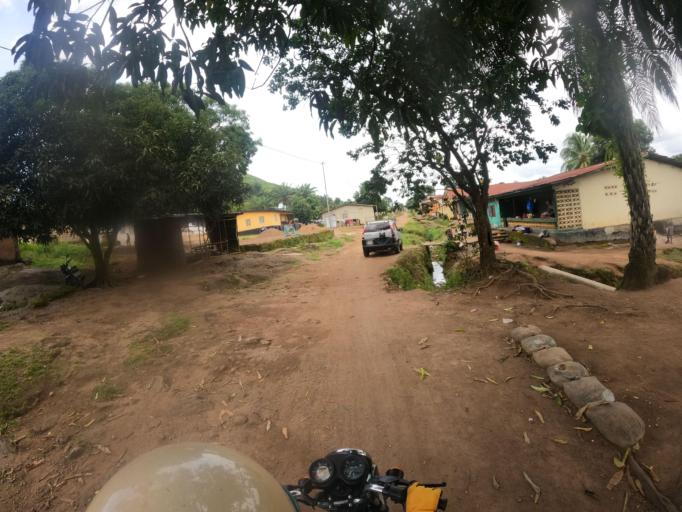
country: SL
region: Northern Province
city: Makeni
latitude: 8.8981
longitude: -12.0458
